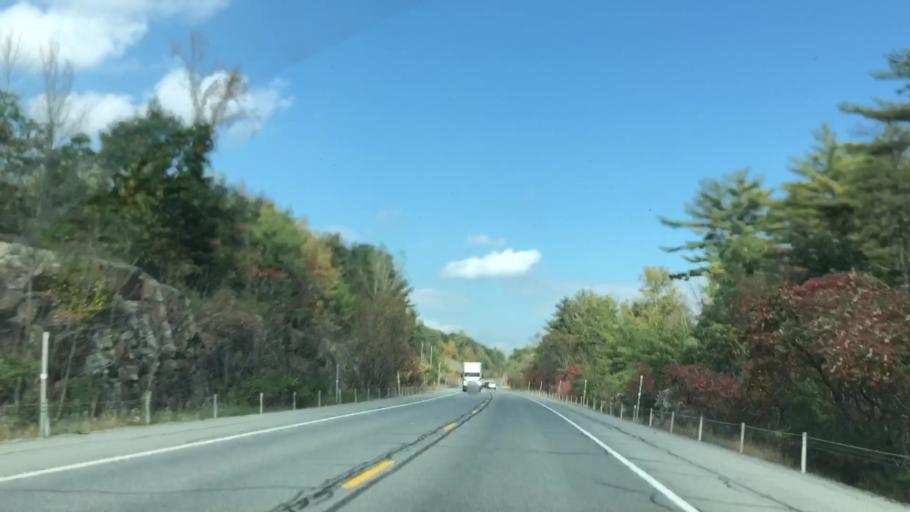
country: US
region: New York
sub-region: Washington County
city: Whitehall
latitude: 43.4474
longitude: -73.4507
